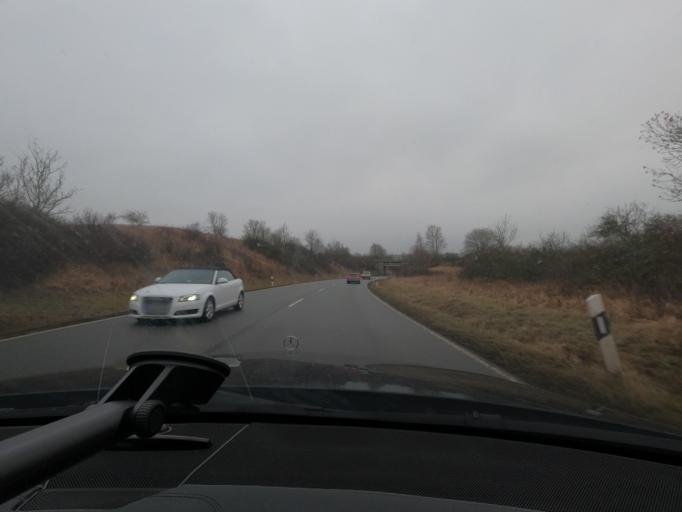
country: DE
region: Hesse
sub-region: Regierungsbezirk Kassel
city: Wolfhagen
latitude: 51.3370
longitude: 9.1420
